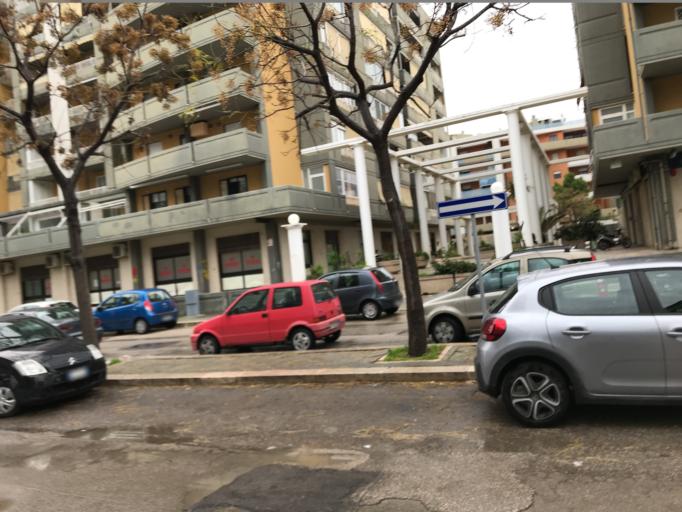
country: IT
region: Apulia
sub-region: Provincia di Bari
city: San Paolo
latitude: 41.1383
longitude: 16.8168
